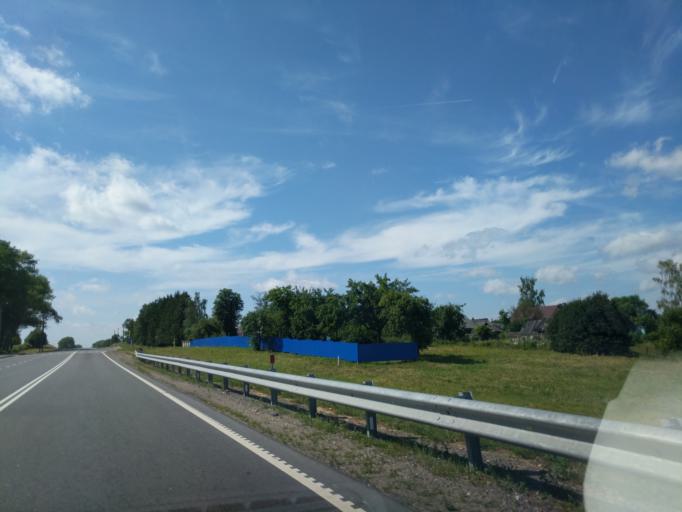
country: BY
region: Minsk
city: Syomkava
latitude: 54.1012
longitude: 27.4814
